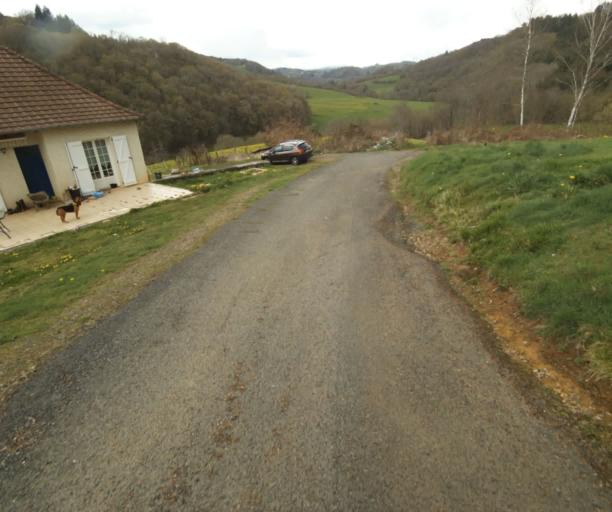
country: FR
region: Limousin
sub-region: Departement de la Correze
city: Naves
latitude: 45.3195
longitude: 1.8098
